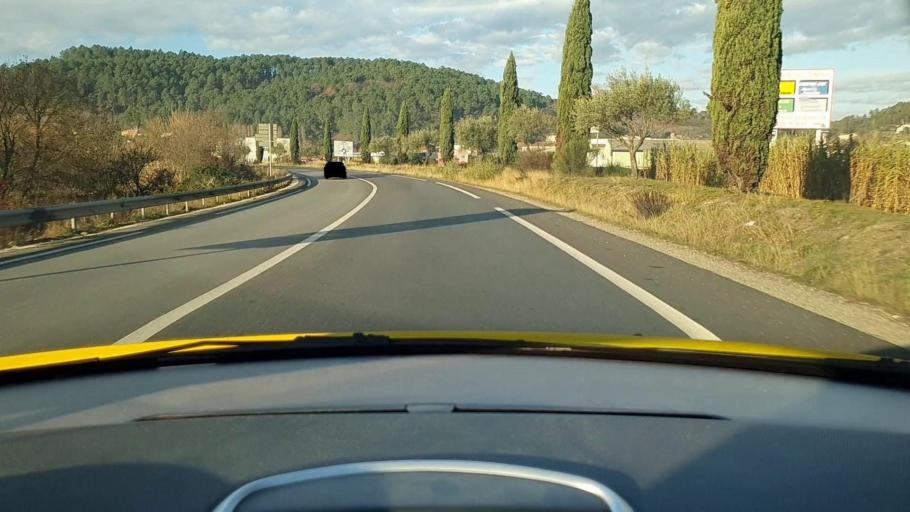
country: FR
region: Languedoc-Roussillon
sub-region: Departement du Gard
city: Saint-Martin-de-Valgalgues
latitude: 44.1582
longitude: 4.0891
